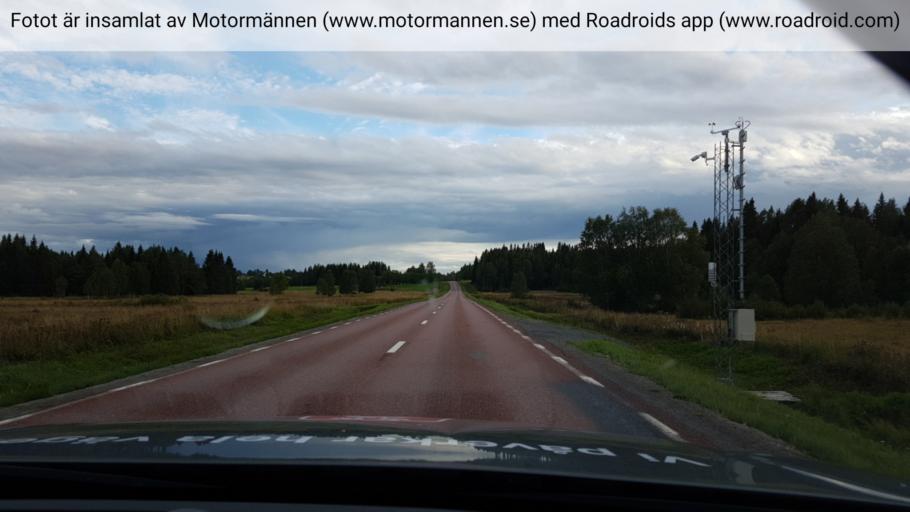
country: SE
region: Jaemtland
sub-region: Stroemsunds Kommun
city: Stroemsund
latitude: 63.7452
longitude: 15.4924
